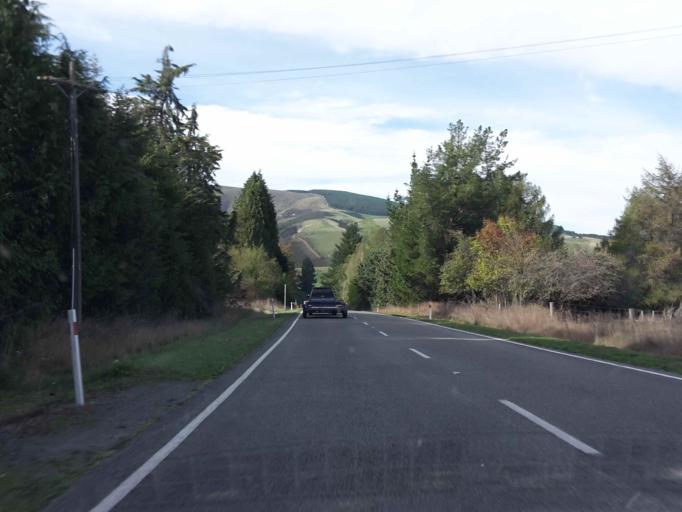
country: NZ
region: Canterbury
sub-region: Timaru District
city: Pleasant Point
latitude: -44.0834
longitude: 170.9713
